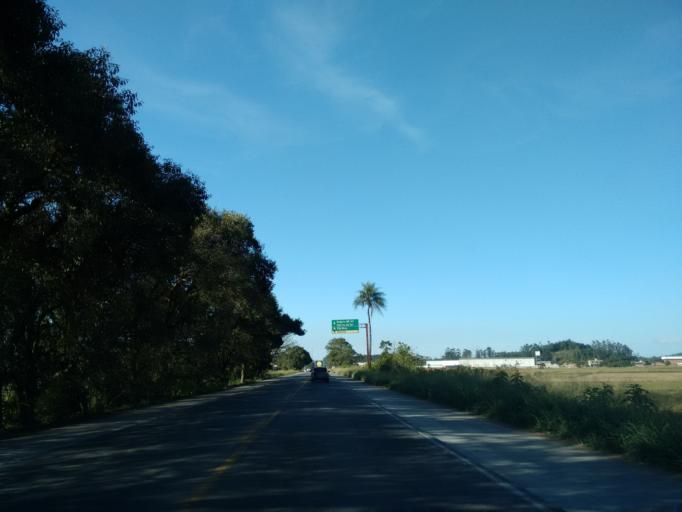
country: BR
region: Santa Catarina
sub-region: Guaramirim
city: Guaramirim
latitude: -26.4695
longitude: -48.9664
